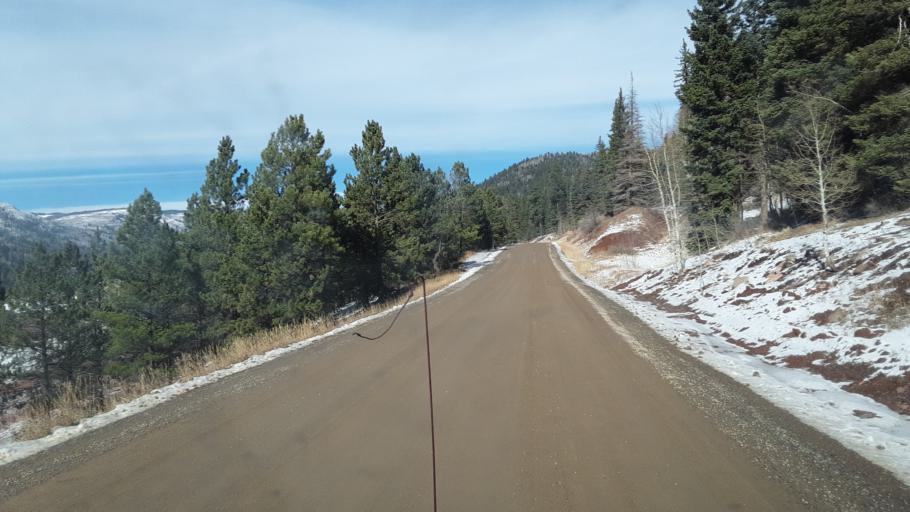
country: US
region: Colorado
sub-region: La Plata County
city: Bayfield
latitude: 37.4011
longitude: -107.6594
